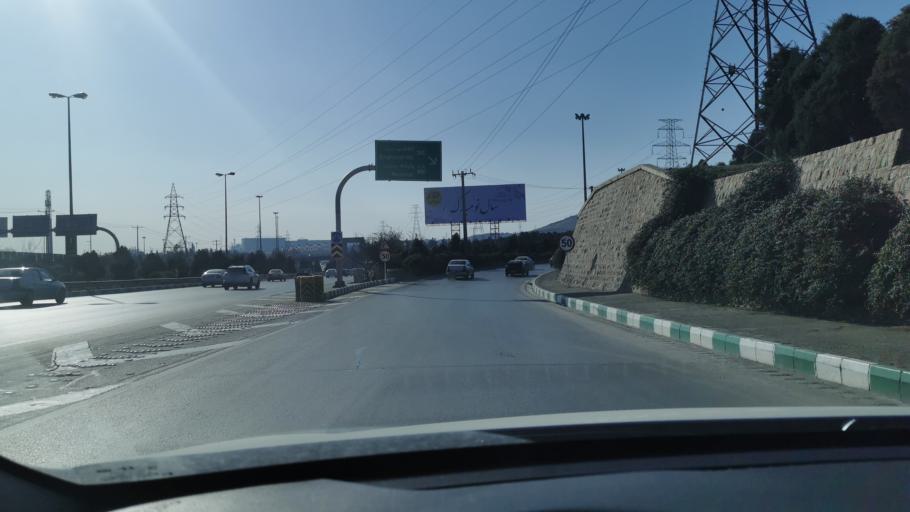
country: IR
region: Razavi Khorasan
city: Mashhad
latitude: 36.2655
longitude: 59.5806
